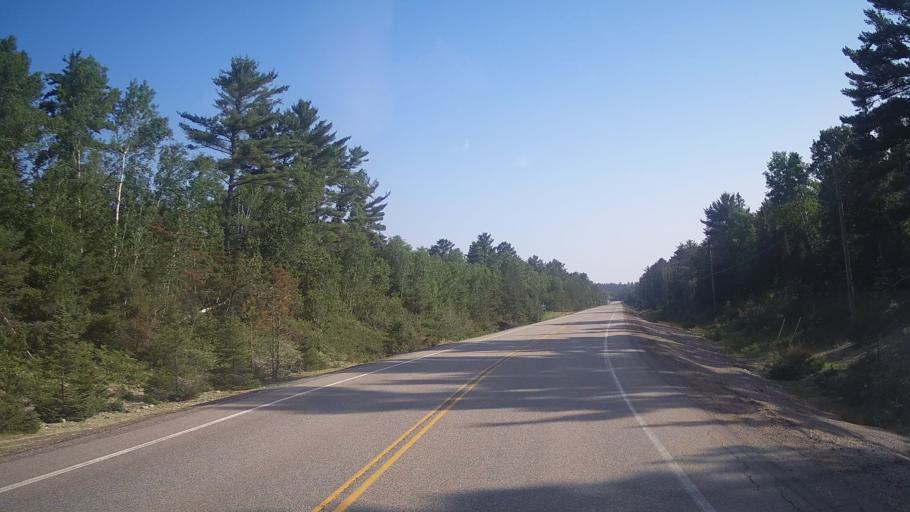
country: CA
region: Ontario
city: Rayside-Balfour
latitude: 46.7476
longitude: -81.6014
